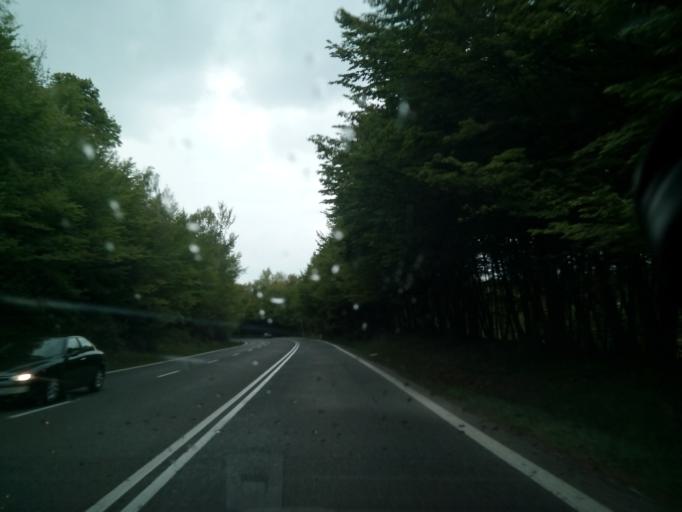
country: SK
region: Kosicky
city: Kosice
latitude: 48.7327
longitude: 21.3796
